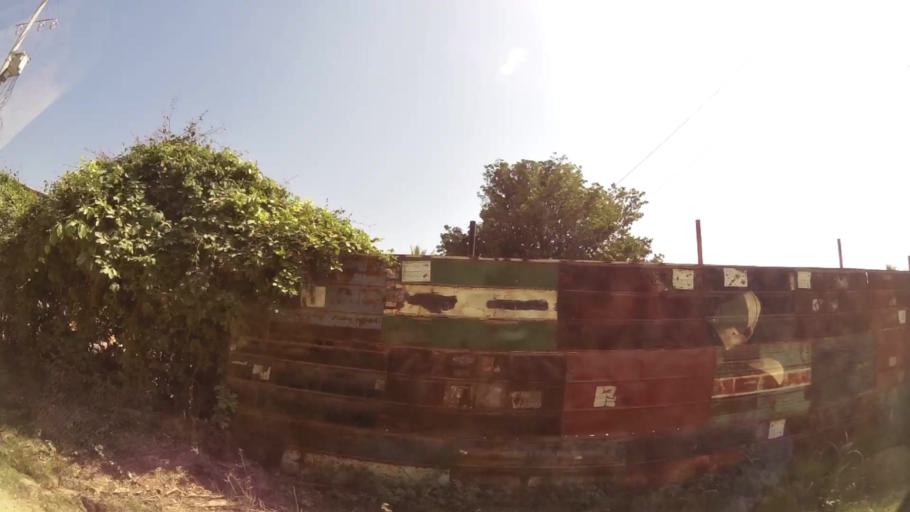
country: CO
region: Bolivar
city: Cartagena
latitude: 10.3600
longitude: -75.4882
